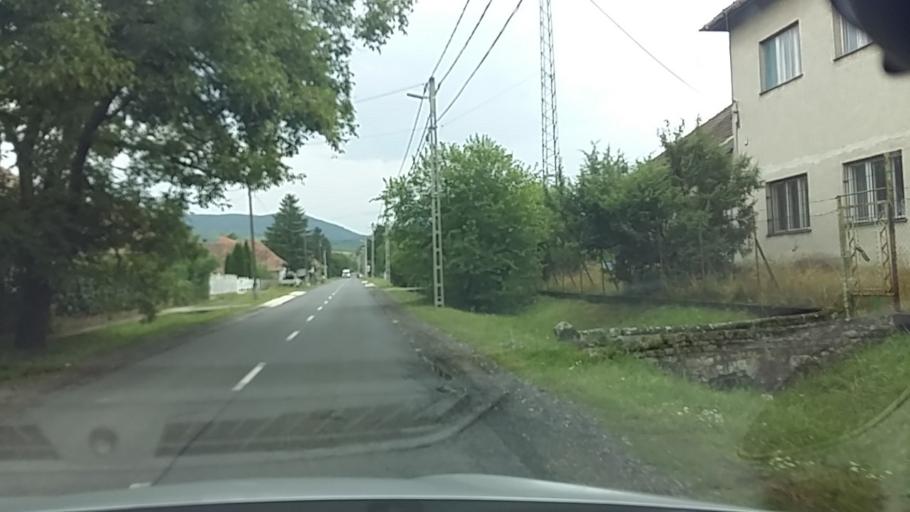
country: HU
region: Komarom-Esztergom
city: Esztergom
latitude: 47.8873
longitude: 18.7702
